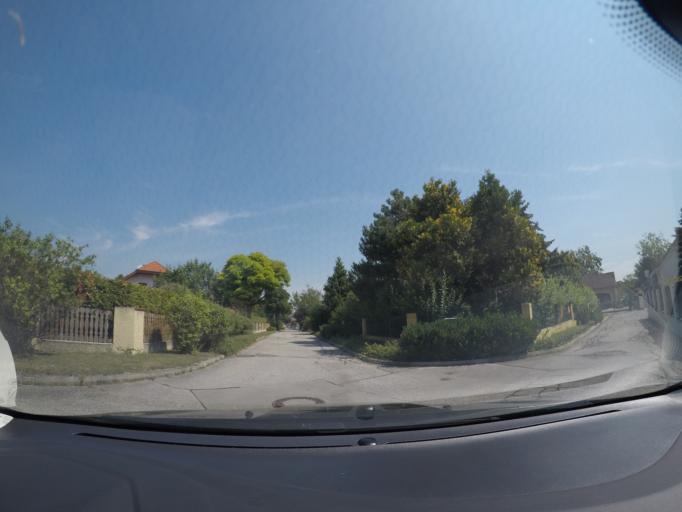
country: AT
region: Lower Austria
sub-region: Politischer Bezirk Baden
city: Tattendorf
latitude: 47.9255
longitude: 16.2984
